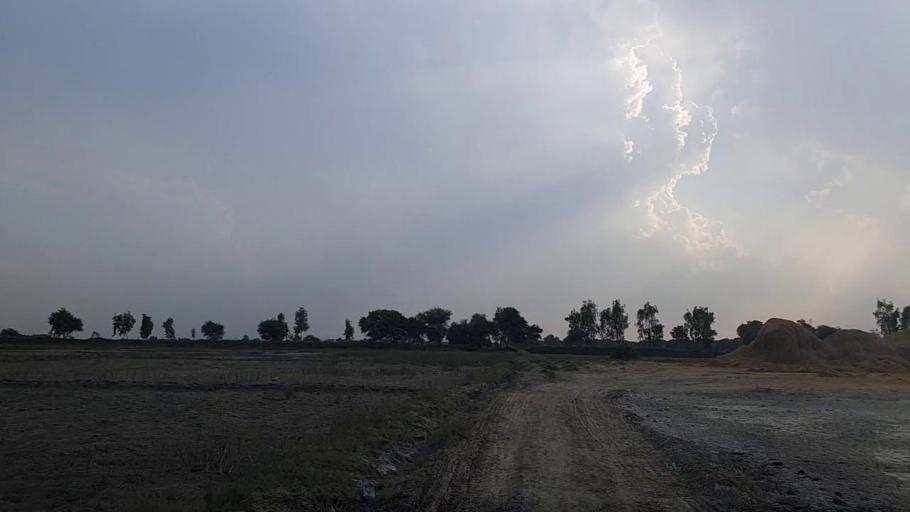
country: PK
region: Sindh
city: Daro Mehar
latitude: 24.7756
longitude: 68.1229
